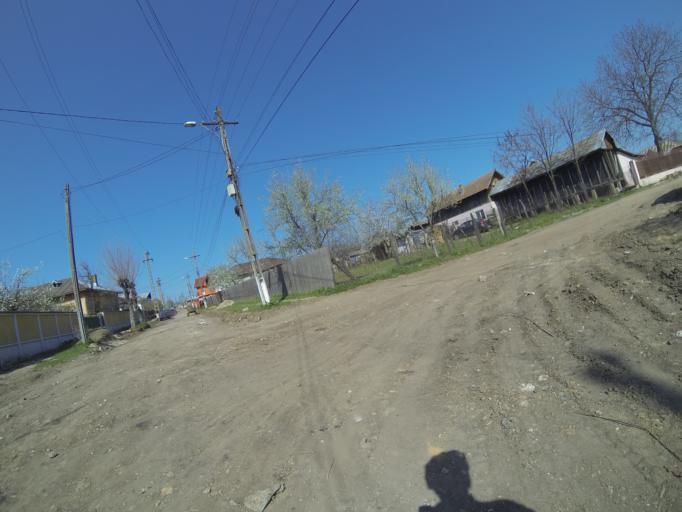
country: RO
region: Dolj
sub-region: Comuna Segarcea
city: Segarcea
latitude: 44.0957
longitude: 23.7344
